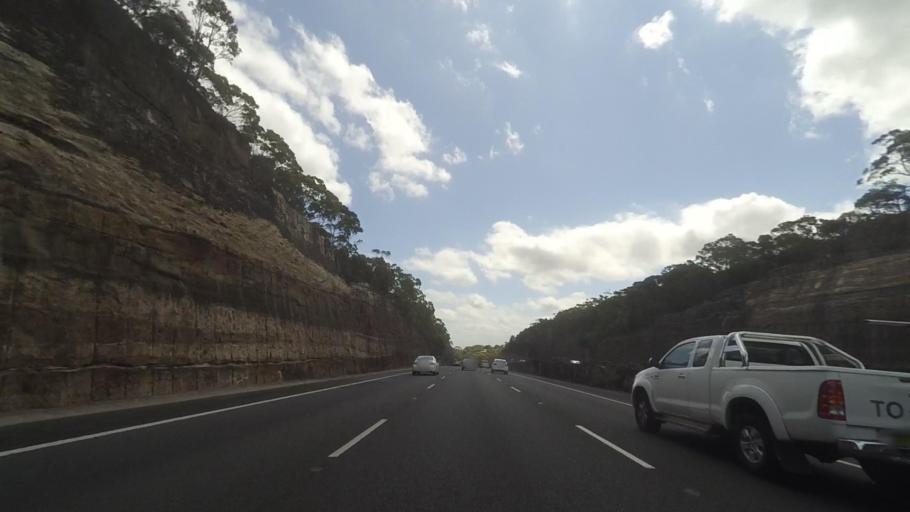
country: AU
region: New South Wales
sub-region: Hornsby Shire
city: Berowra
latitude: -33.5860
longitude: 151.1812
